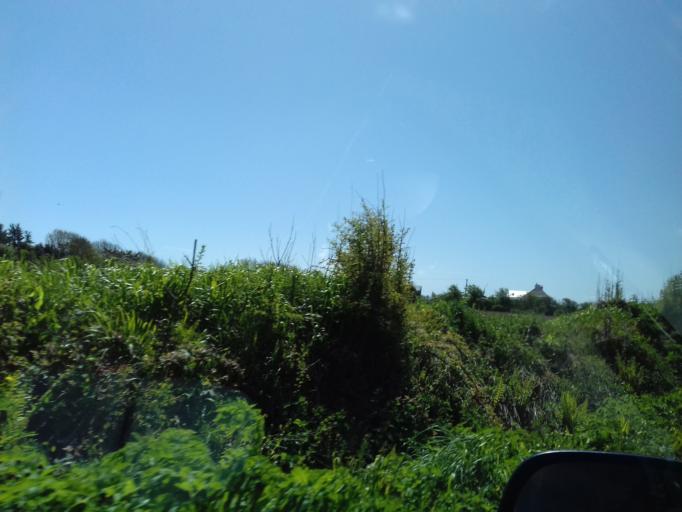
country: IE
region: Munster
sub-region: Waterford
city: Dunmore East
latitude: 52.1895
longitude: -6.8564
